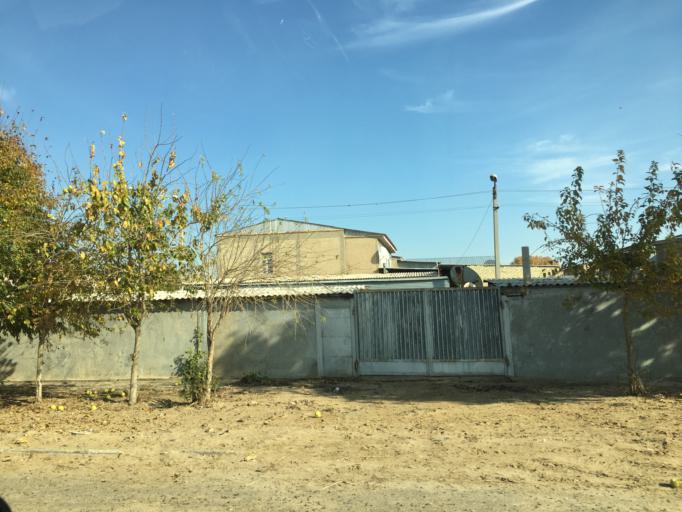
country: TM
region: Mary
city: Mary
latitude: 37.5959
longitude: 61.5829
